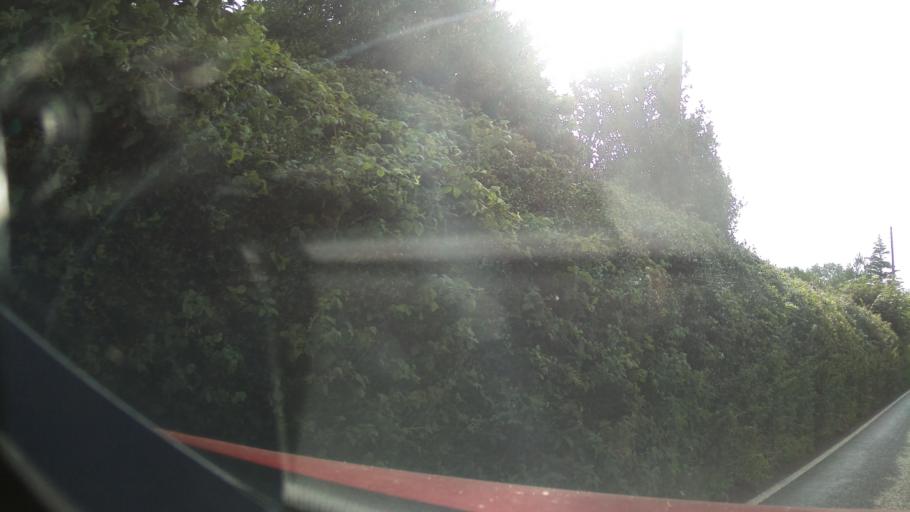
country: GB
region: England
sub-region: North Somerset
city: Nailsea
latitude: 51.4368
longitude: -2.7224
